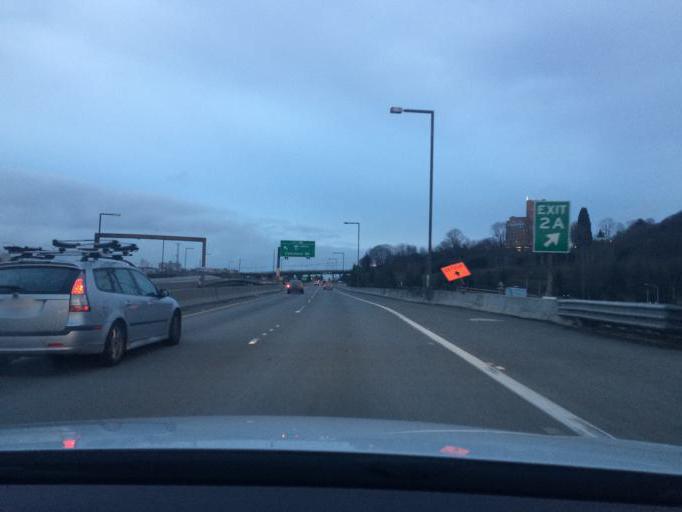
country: US
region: Washington
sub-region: King County
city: Seattle
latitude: 47.5925
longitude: -122.3248
